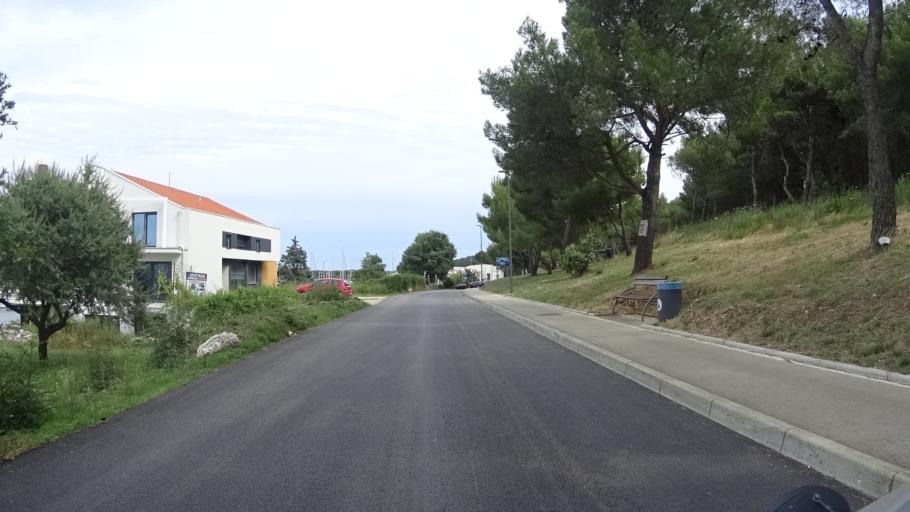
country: HR
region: Istarska
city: Medulin
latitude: 44.8226
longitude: 13.9000
